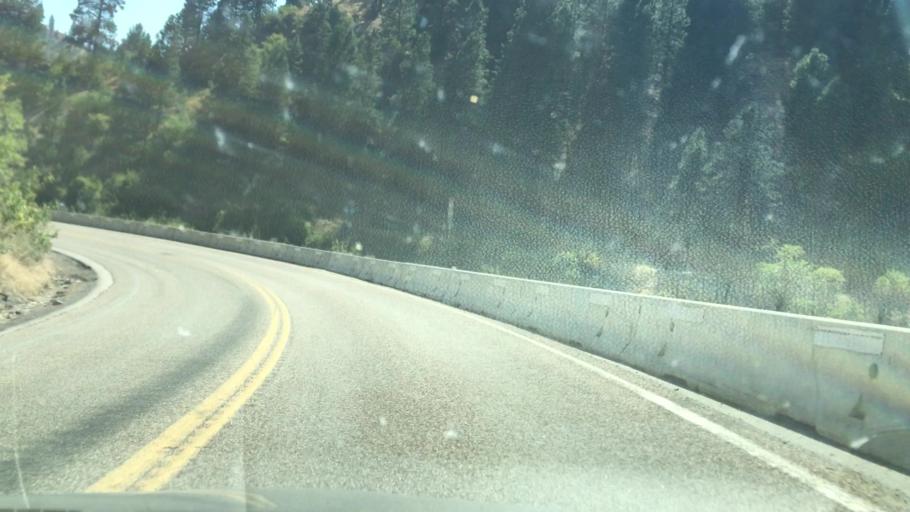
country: US
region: Idaho
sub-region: Boise County
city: Idaho City
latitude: 44.0990
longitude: -116.0994
